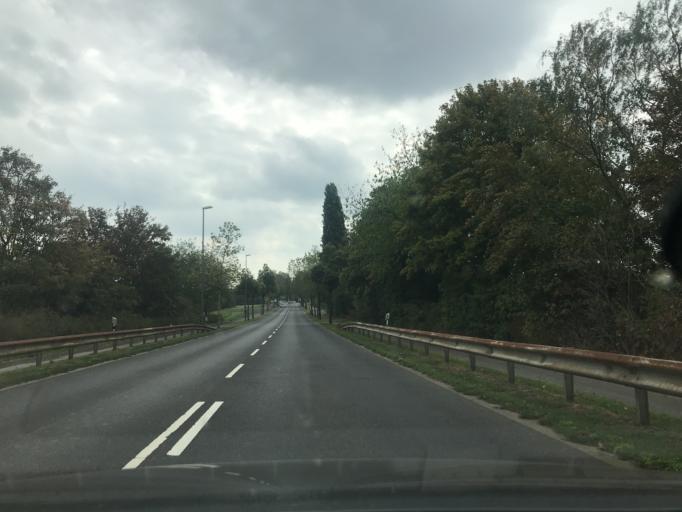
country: DE
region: North Rhine-Westphalia
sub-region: Regierungsbezirk Dusseldorf
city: Krefeld
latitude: 51.3717
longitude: 6.6358
